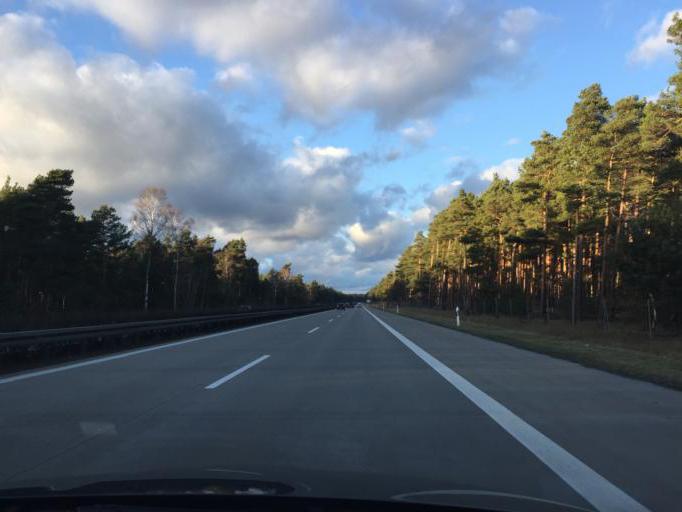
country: DE
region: Brandenburg
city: Halbe
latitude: 52.0404
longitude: 13.6681
